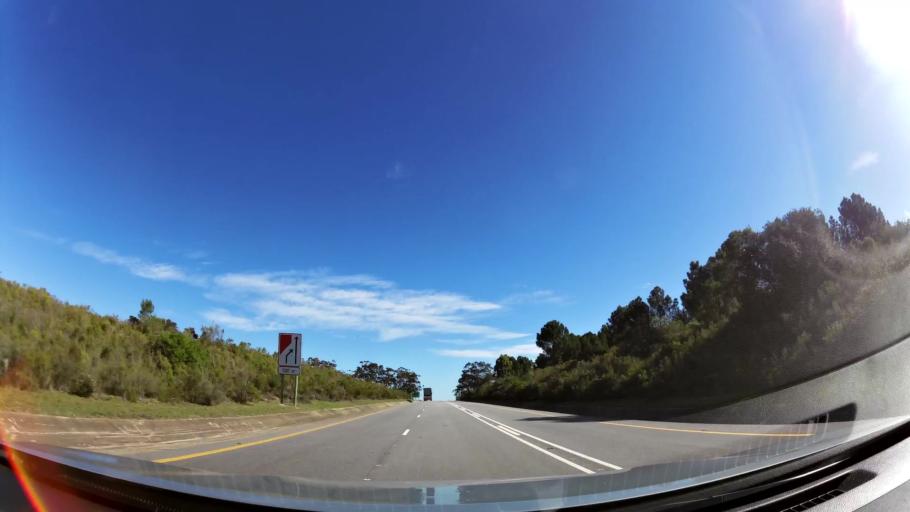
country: ZA
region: Eastern Cape
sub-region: Cacadu District Municipality
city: Kruisfontein
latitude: -34.0191
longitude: 24.6203
